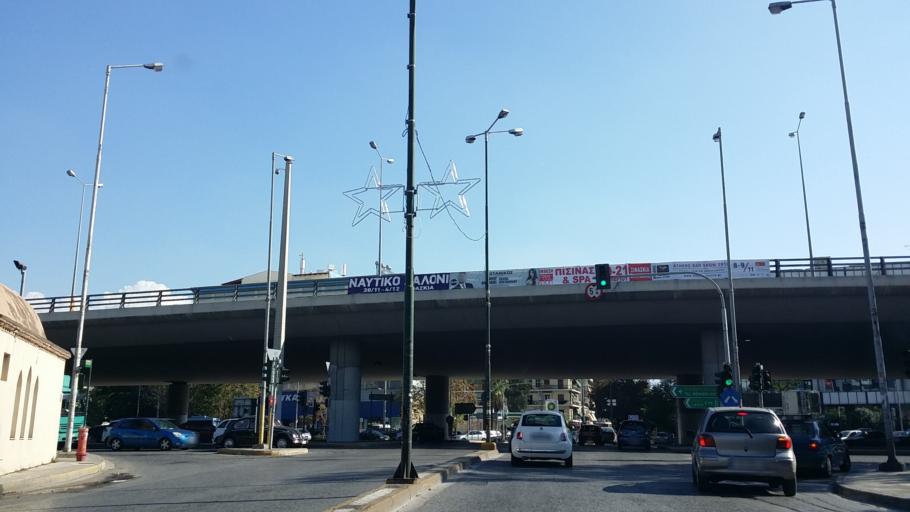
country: GR
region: Attica
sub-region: Nomarchia Athinas
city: Agioi Anargyroi
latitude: 38.0088
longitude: 23.7145
